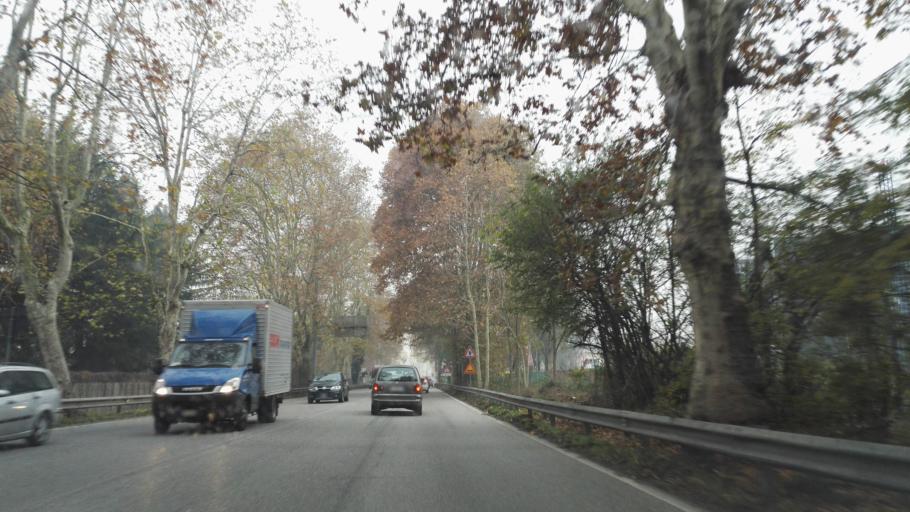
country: IT
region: Lombardy
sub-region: Citta metropolitana di Milano
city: Novegro-Tregarezzo-San Felice
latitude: 45.4651
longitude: 9.2832
